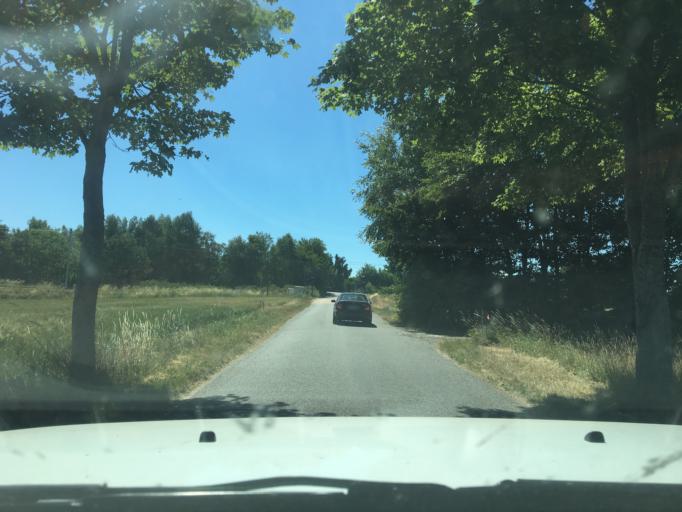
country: DK
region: Central Jutland
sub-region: Syddjurs Kommune
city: Hornslet
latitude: 56.3428
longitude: 10.3855
